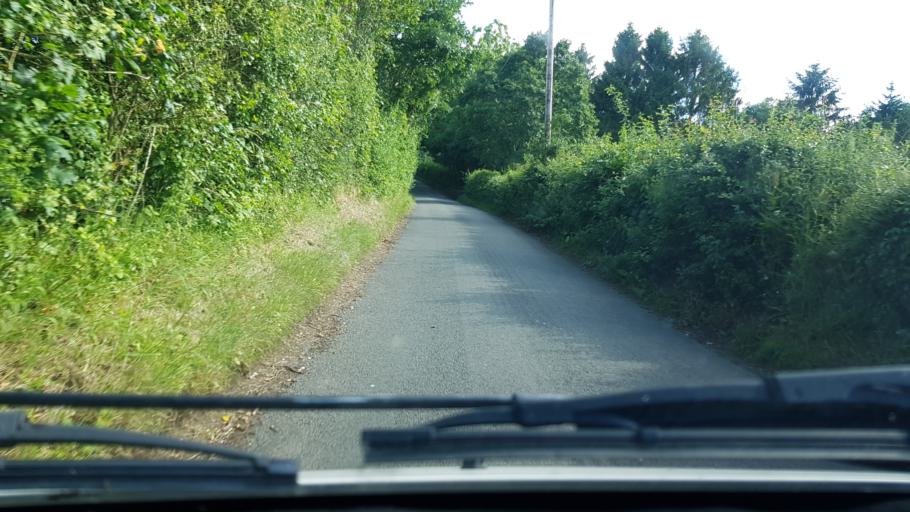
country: GB
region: England
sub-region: Worcestershire
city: Bewdley
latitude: 52.3641
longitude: -2.3248
